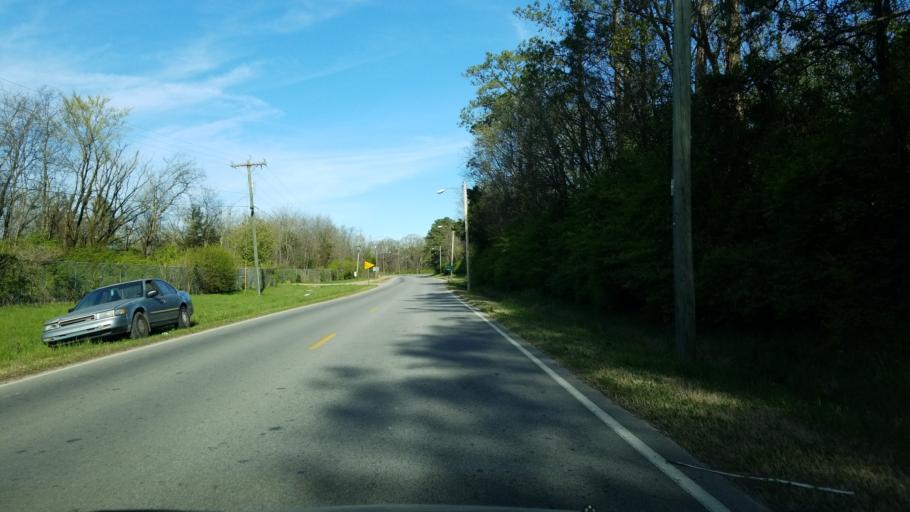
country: US
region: Tennessee
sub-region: Hamilton County
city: East Chattanooga
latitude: 35.0476
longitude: -85.2031
